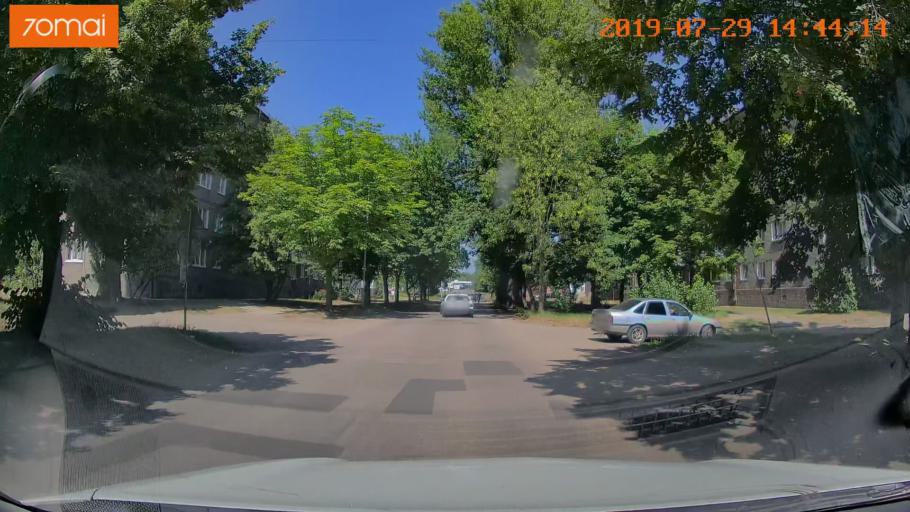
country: RU
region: Kaliningrad
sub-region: Gorod Kaliningrad
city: Baltiysk
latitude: 54.6616
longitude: 19.9085
